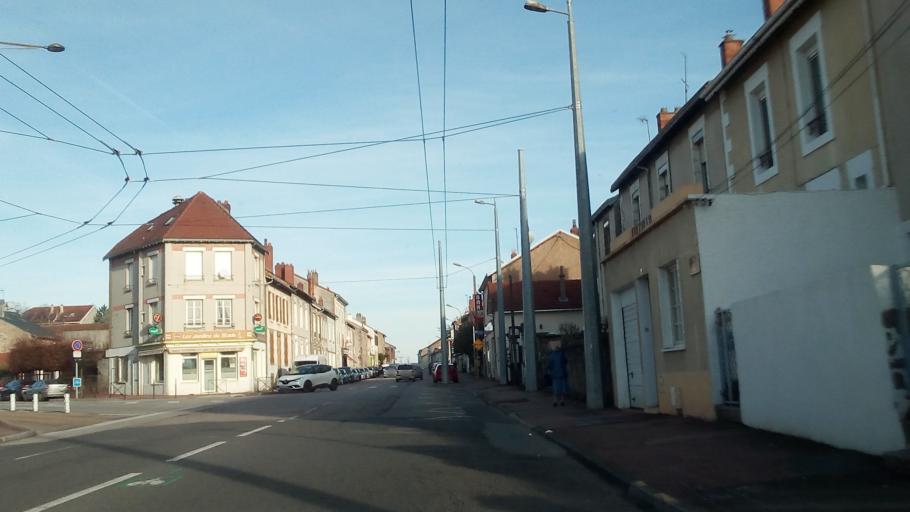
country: FR
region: Limousin
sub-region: Departement de la Haute-Vienne
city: Limoges
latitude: 45.8448
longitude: 1.2456
